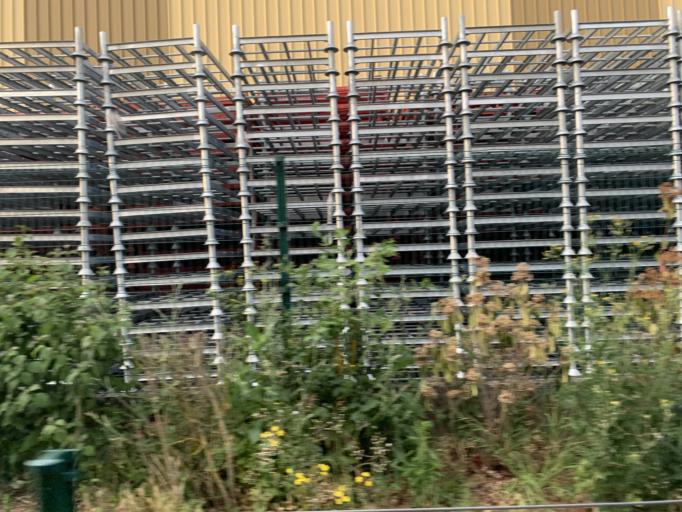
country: FR
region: Rhone-Alpes
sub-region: Departement du Rhone
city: Meyzieu
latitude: 45.7677
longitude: 5.0310
